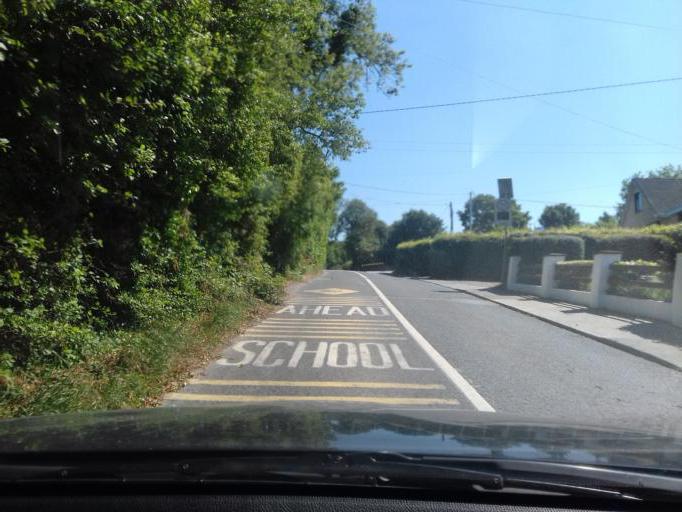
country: IE
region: Leinster
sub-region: An Mhi
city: Stamullin
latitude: 53.5799
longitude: -6.2851
